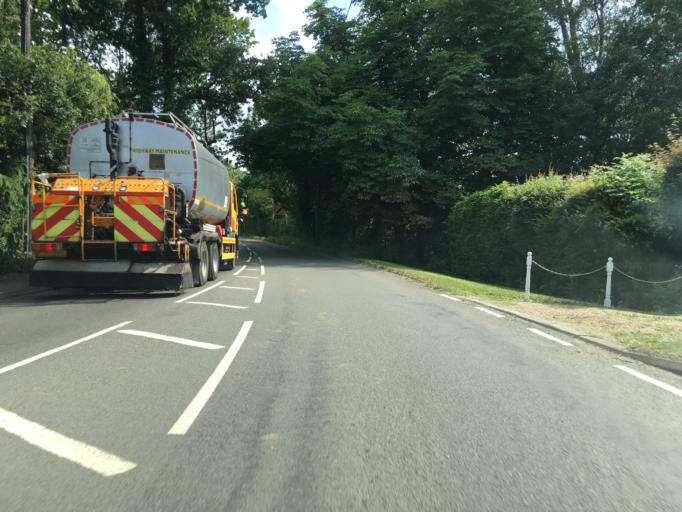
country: GB
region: England
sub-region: Kent
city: Headcorn
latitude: 51.1128
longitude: 0.6431
